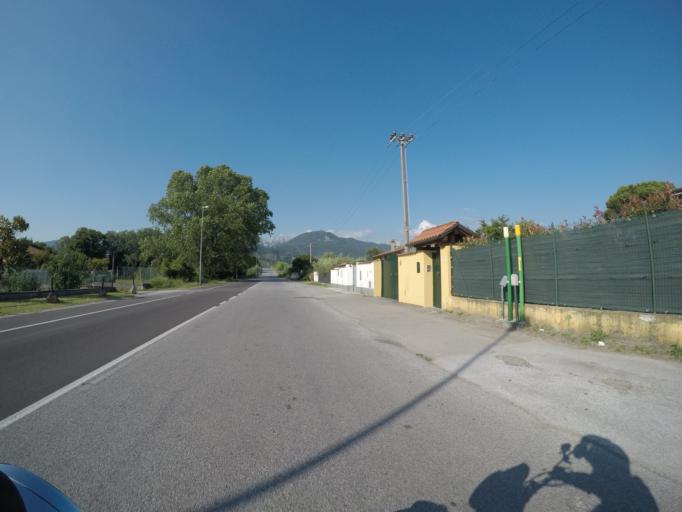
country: IT
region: Tuscany
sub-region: Provincia di Massa-Carrara
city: Carrara
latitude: 44.0300
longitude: 10.0832
